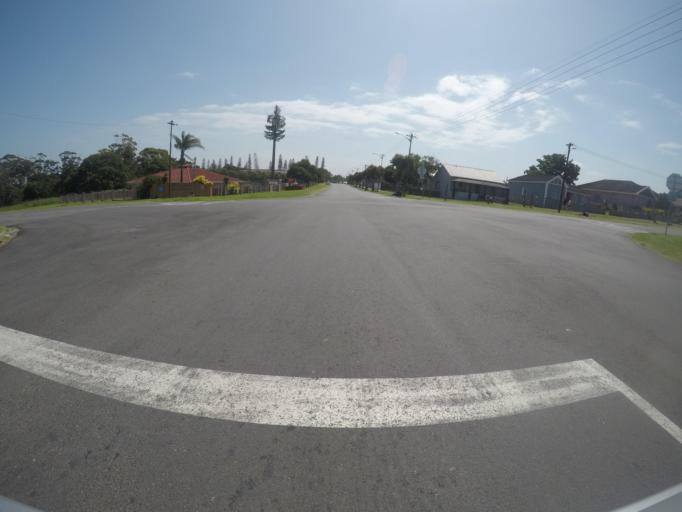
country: ZA
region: Eastern Cape
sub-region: Buffalo City Metropolitan Municipality
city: East London
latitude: -32.9809
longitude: 27.8858
